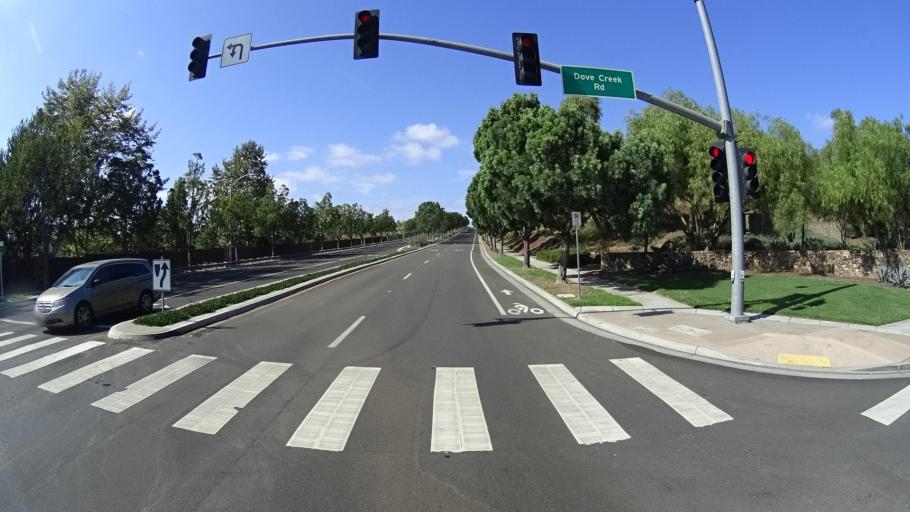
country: US
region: California
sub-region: San Diego County
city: Fairbanks Ranch
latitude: 33.0056
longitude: -117.1089
